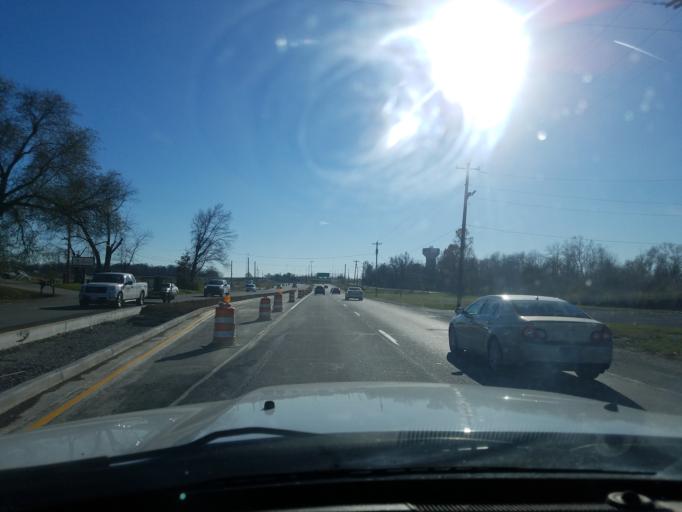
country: US
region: Indiana
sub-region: Clark County
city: Oak Park
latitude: 38.3514
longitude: -85.7044
